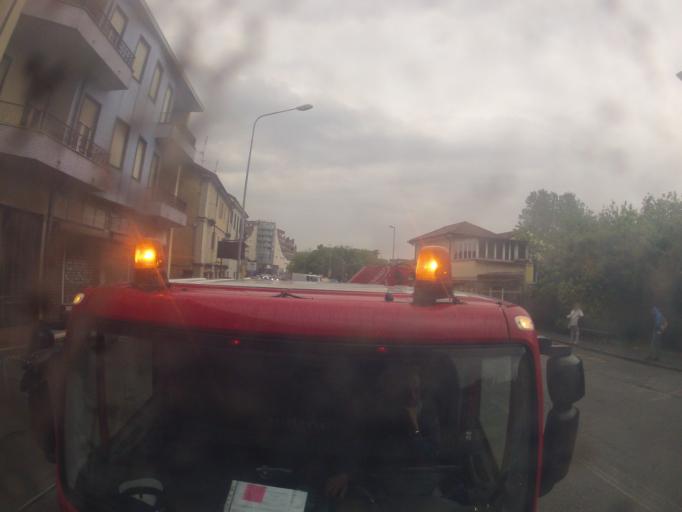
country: IT
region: Piedmont
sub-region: Provincia di Torino
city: Moncalieri
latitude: 45.0008
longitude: 7.6717
